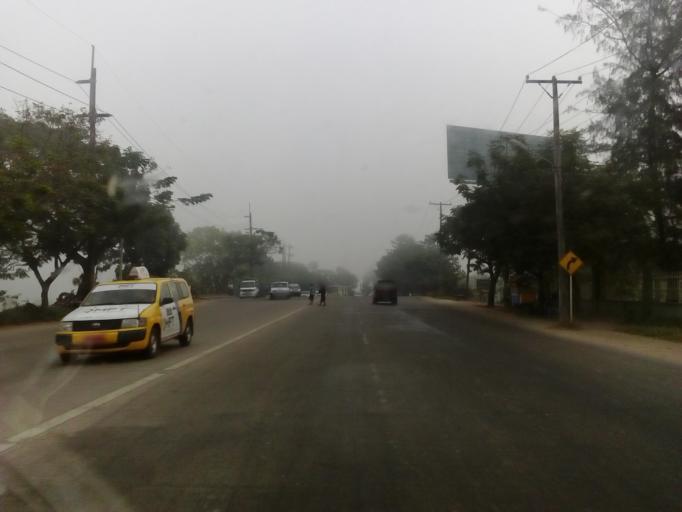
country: MM
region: Yangon
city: Yangon
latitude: 16.8115
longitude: 96.1846
